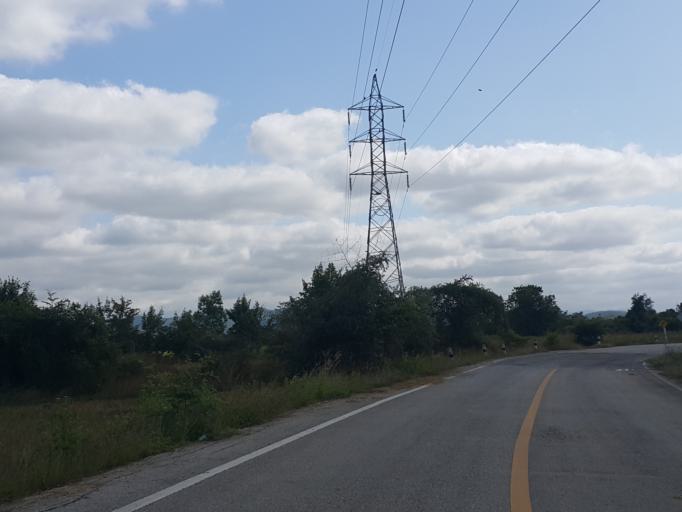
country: TH
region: Lamphun
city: Lamphun
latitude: 18.5439
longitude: 99.0873
